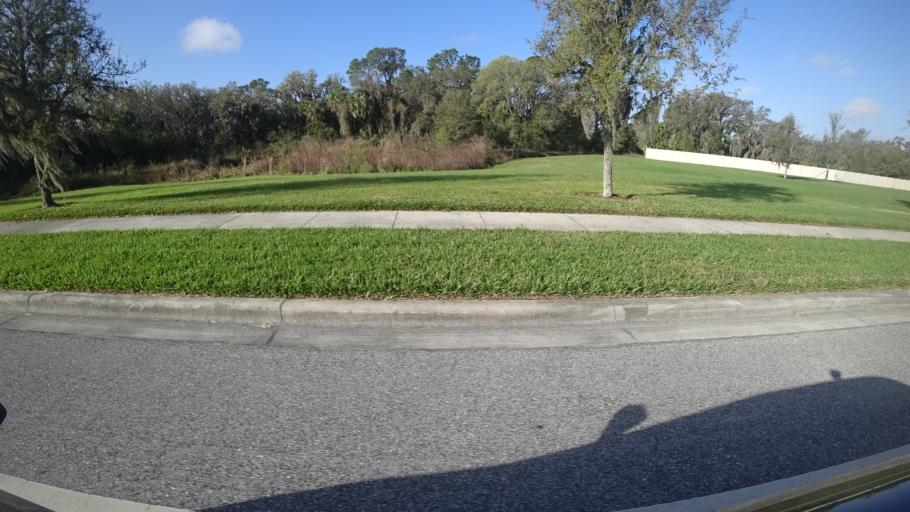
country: US
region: Florida
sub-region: Manatee County
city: Ellenton
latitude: 27.5717
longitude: -82.4681
